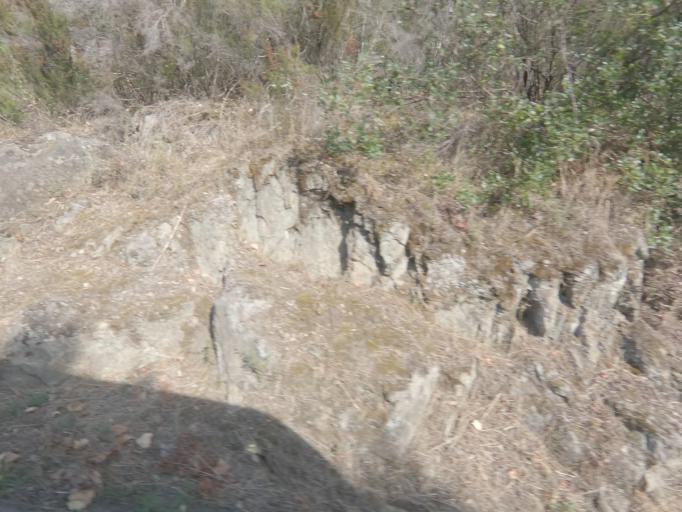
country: PT
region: Vila Real
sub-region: Sabrosa
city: Vilela
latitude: 41.1992
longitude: -7.5428
